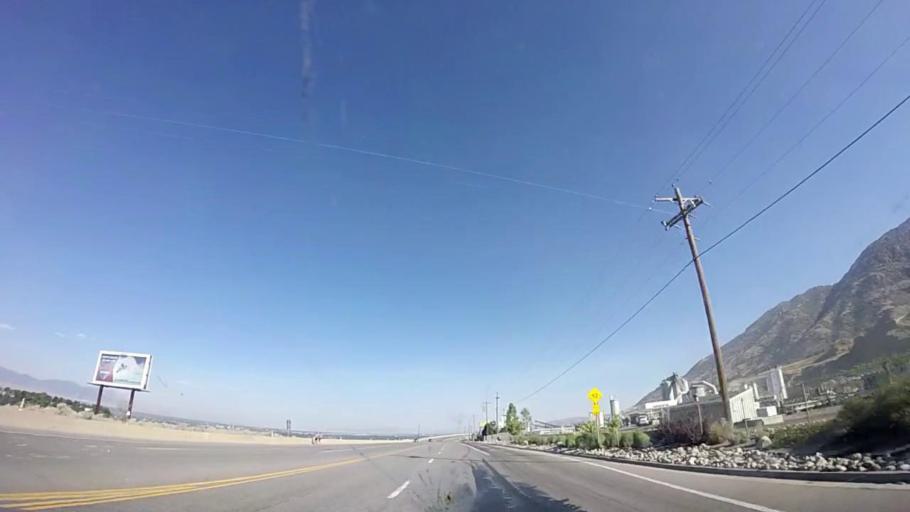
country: US
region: Utah
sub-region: Salt Lake County
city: Cottonwood Heights
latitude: 40.6262
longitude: -111.7972
